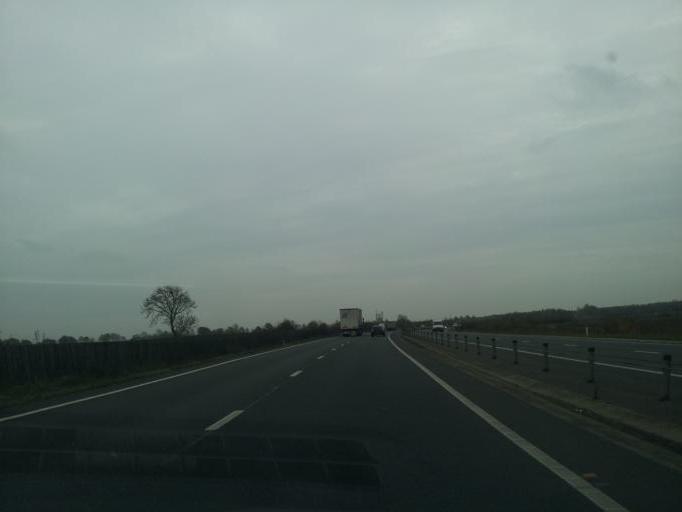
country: GB
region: England
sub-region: Cambridgeshire
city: Papworth Everard
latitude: 52.2286
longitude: -0.0860
